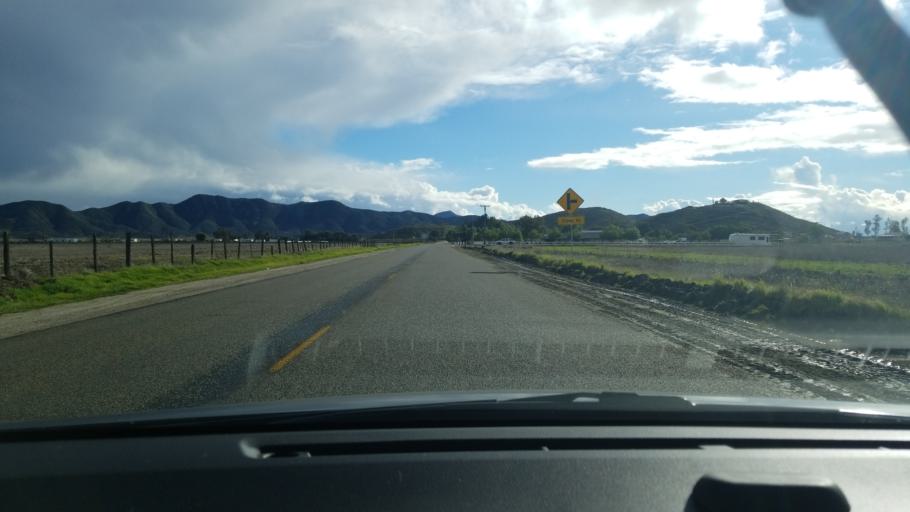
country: US
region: California
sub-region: Riverside County
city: Green Acres
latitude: 33.7237
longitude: -117.0501
